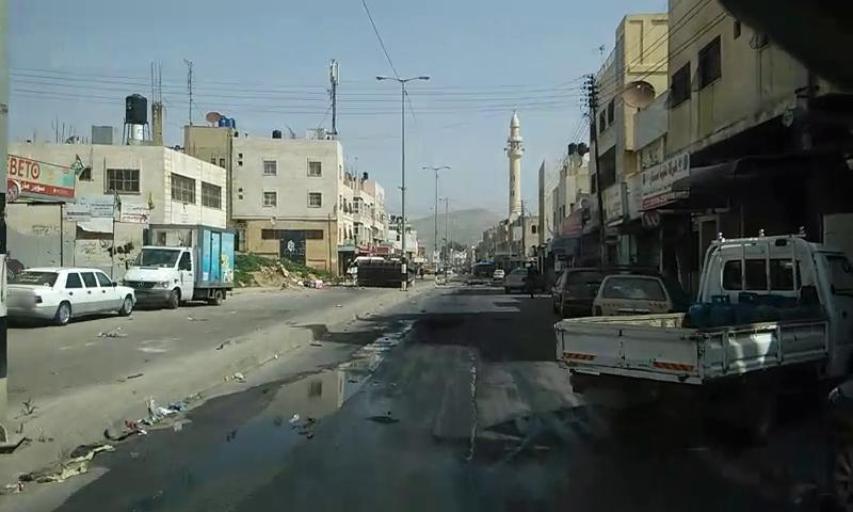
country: PS
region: West Bank
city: Balatah
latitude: 32.2197
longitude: 35.2955
